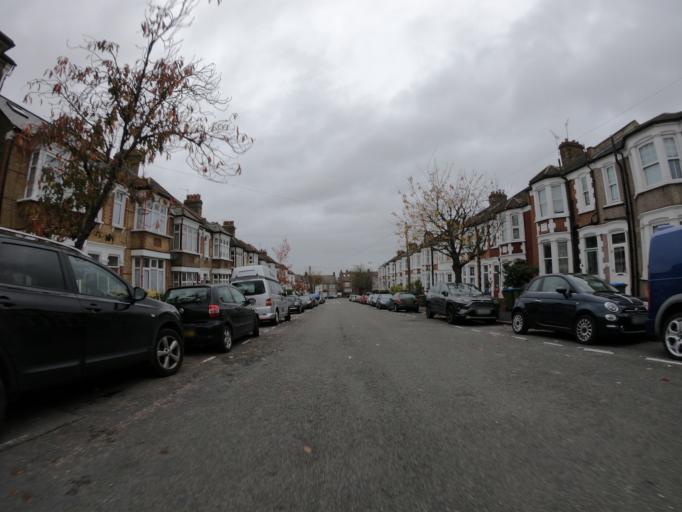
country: GB
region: England
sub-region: Greater London
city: Blackheath
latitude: 51.4804
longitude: 0.0244
